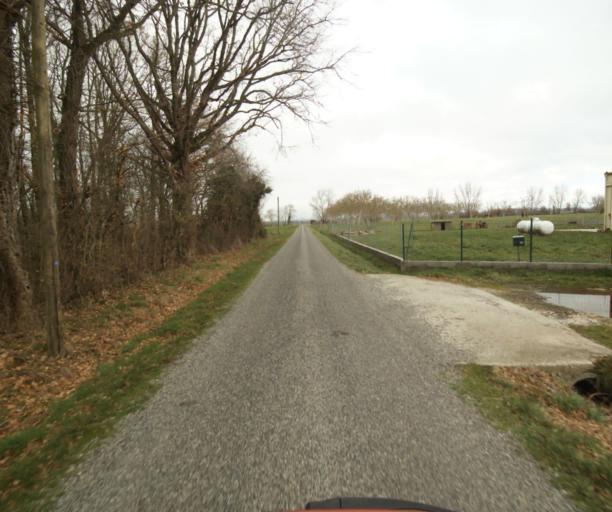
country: FR
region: Languedoc-Roussillon
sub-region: Departement de l'Aude
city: Belpech
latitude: 43.1814
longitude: 1.6865
